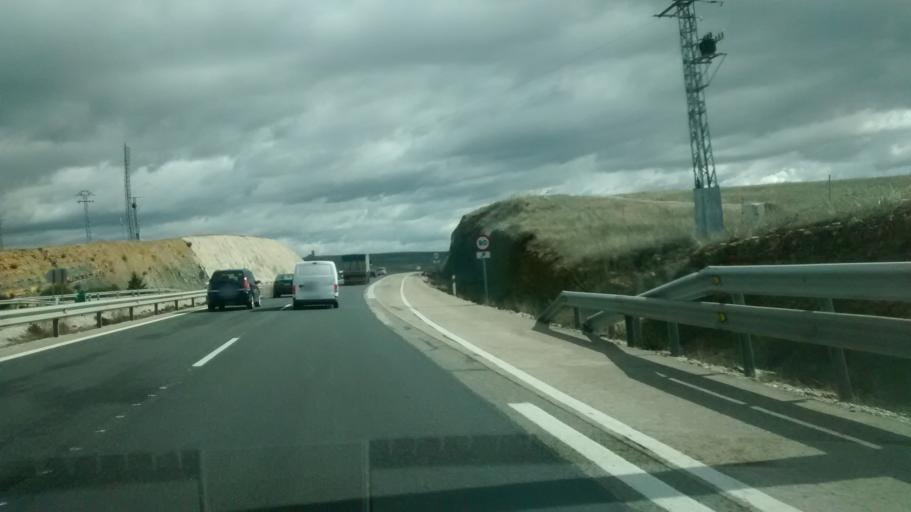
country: ES
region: Castille-La Mancha
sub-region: Provincia de Guadalajara
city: Torremocha del Campo
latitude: 40.9724
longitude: -2.6247
